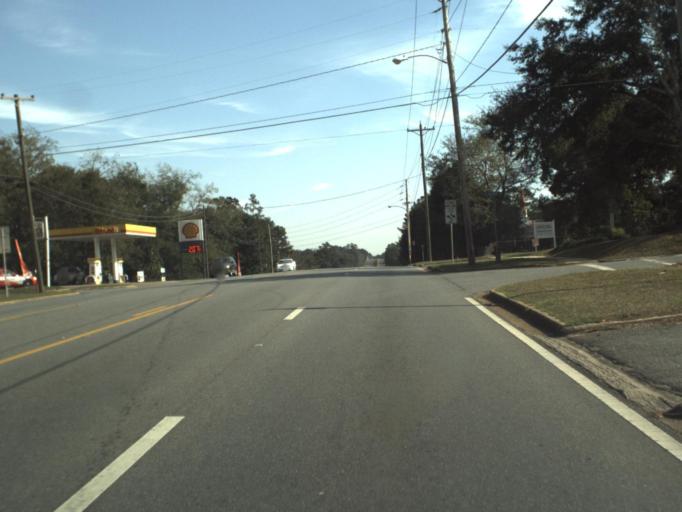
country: US
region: Florida
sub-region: Gadsden County
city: Quincy
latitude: 30.5838
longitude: -84.5645
